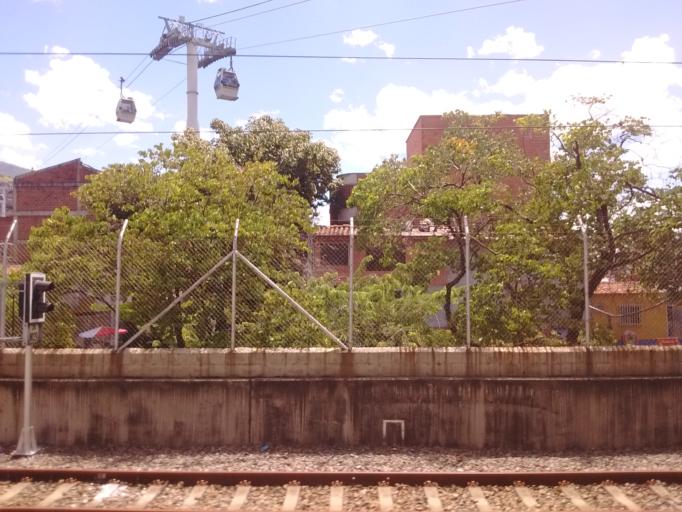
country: CO
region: Antioquia
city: Medellin
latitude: 6.2569
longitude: -75.6136
